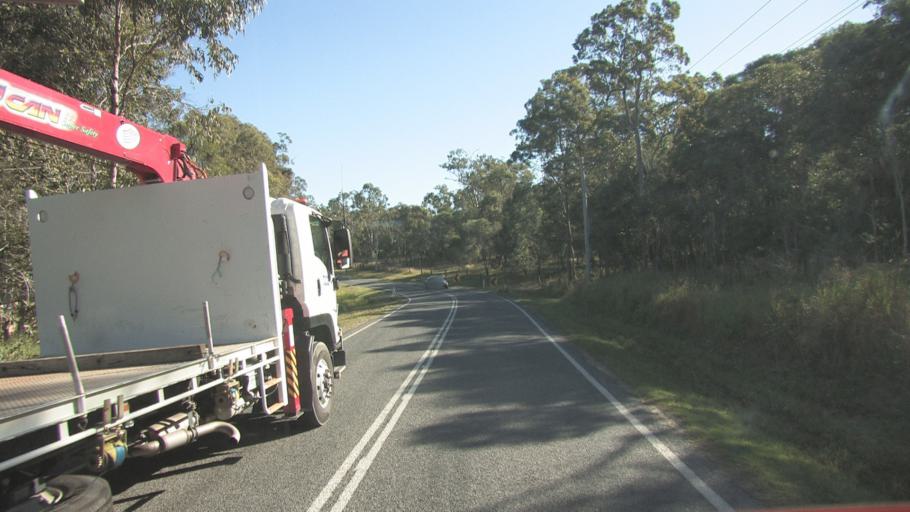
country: AU
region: Queensland
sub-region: Logan
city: Windaroo
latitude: -27.7350
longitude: 153.1598
